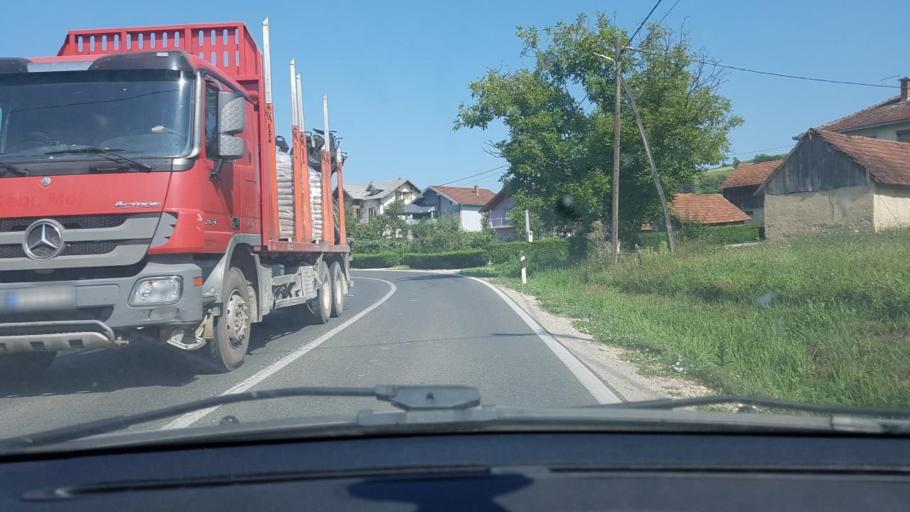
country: BA
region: Federation of Bosnia and Herzegovina
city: Mala Kladusa
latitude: 45.1318
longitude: 15.8625
